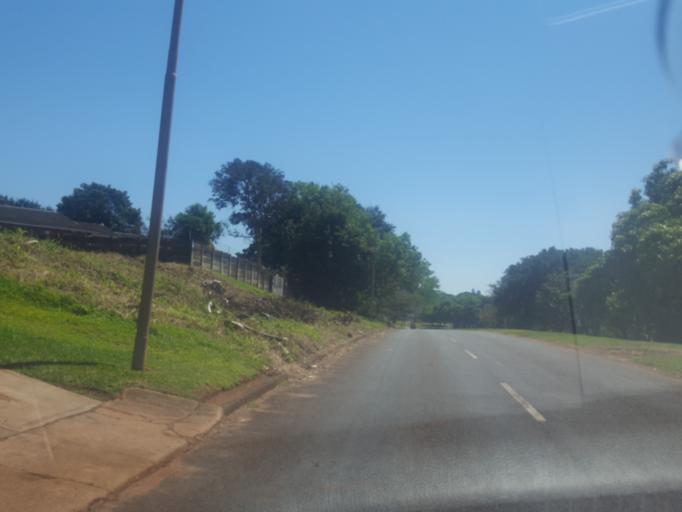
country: ZA
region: KwaZulu-Natal
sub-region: uThungulu District Municipality
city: Empangeni
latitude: -28.7560
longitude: 31.9061
